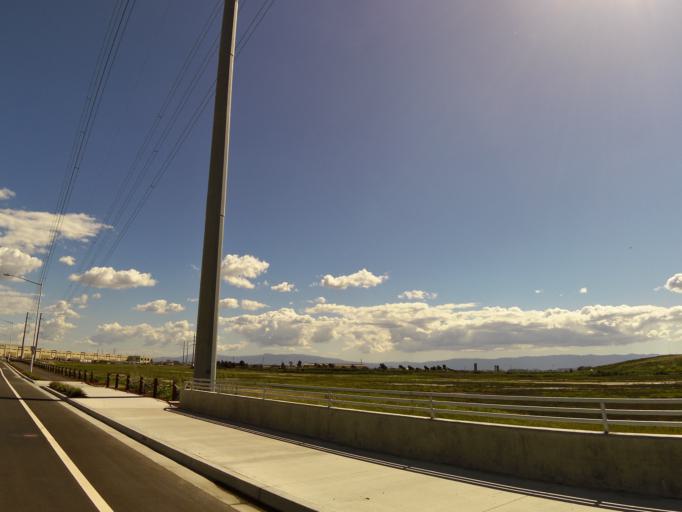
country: US
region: California
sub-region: Santa Clara County
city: Milpitas
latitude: 37.4619
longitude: -121.9288
